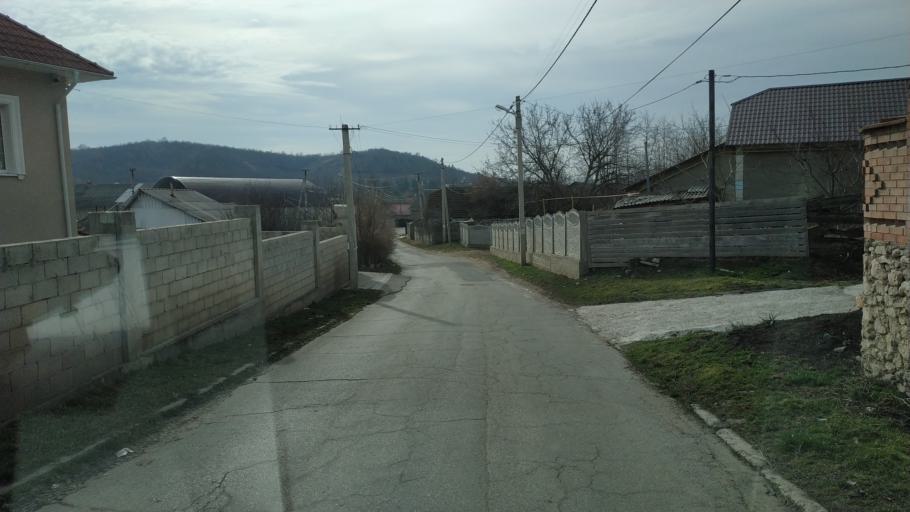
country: MD
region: Chisinau
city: Vatra
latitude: 47.0903
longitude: 28.7689
